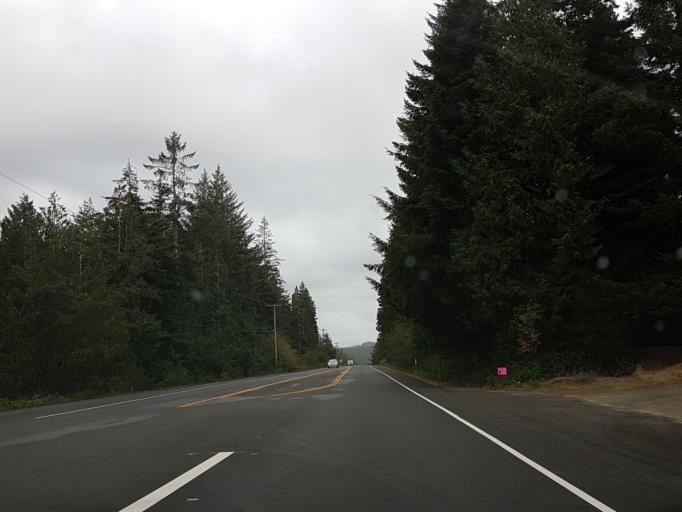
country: US
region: Oregon
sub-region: Lane County
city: Dunes City
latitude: 43.8954
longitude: -124.1180
